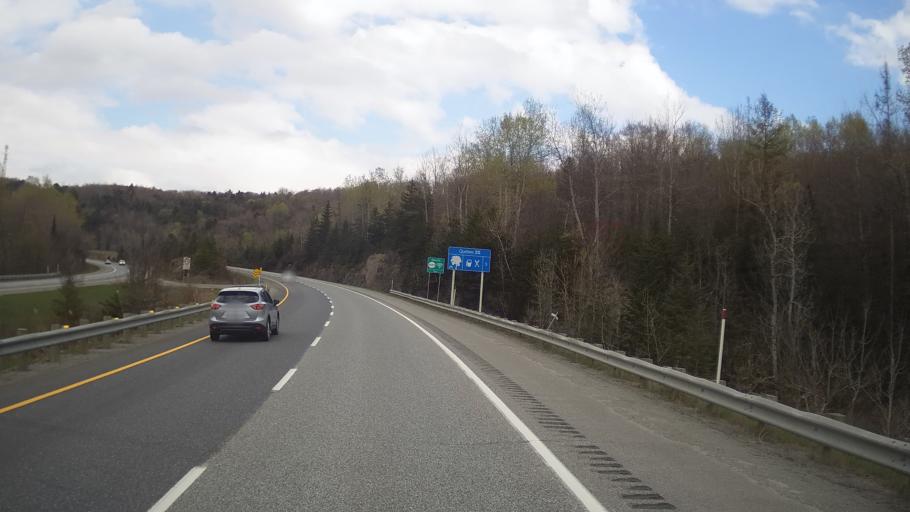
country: CA
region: Quebec
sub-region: Estrie
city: Magog
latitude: 45.2857
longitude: -72.2799
